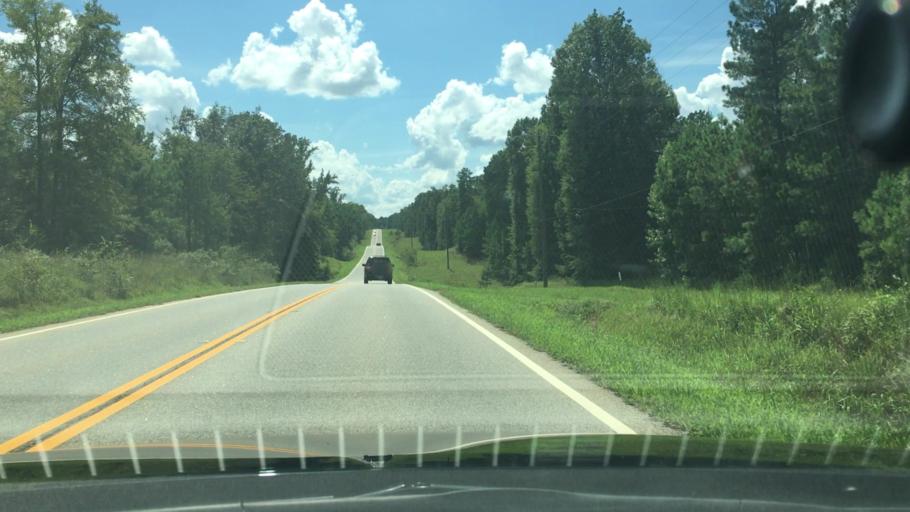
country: US
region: Georgia
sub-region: Putnam County
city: Eatonton
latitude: 33.3103
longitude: -83.4648
